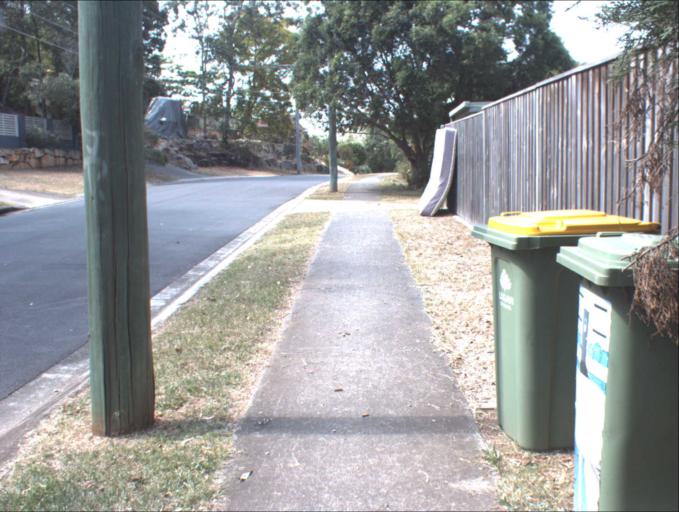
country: AU
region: Queensland
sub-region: Logan
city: Slacks Creek
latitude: -27.6580
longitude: 153.1899
